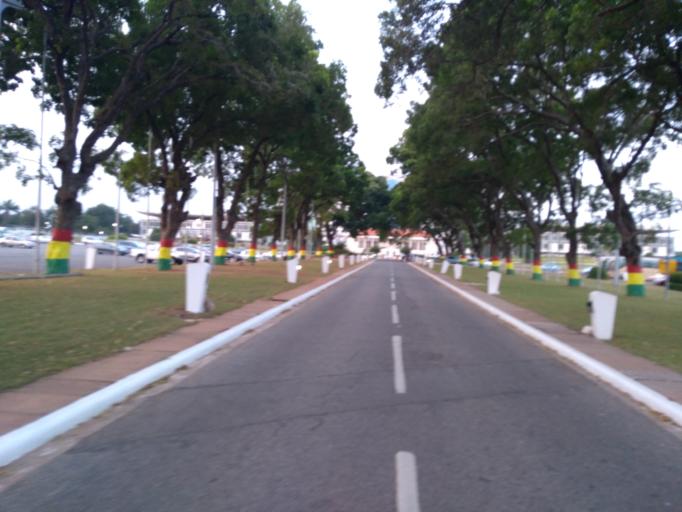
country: GH
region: Greater Accra
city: Accra
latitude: 5.5557
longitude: -0.1921
